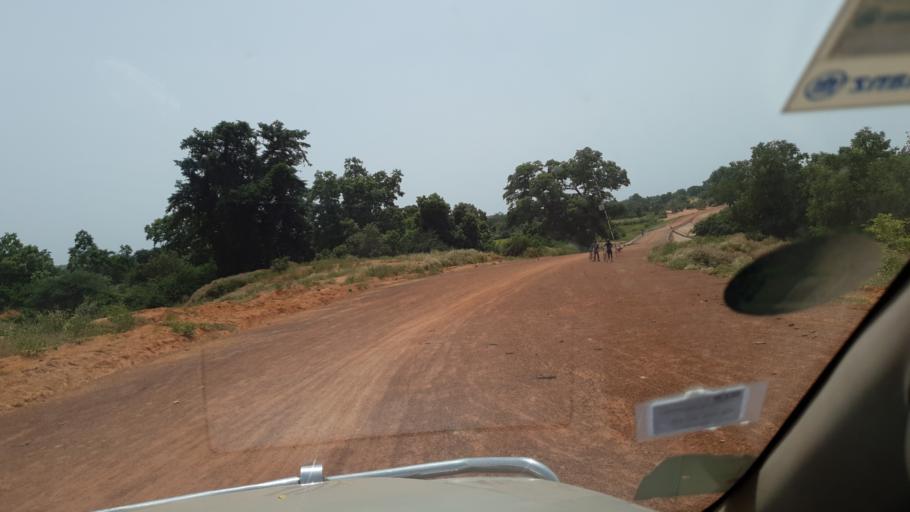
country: ML
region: Koulikoro
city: Kolokani
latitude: 13.4251
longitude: -8.2405
